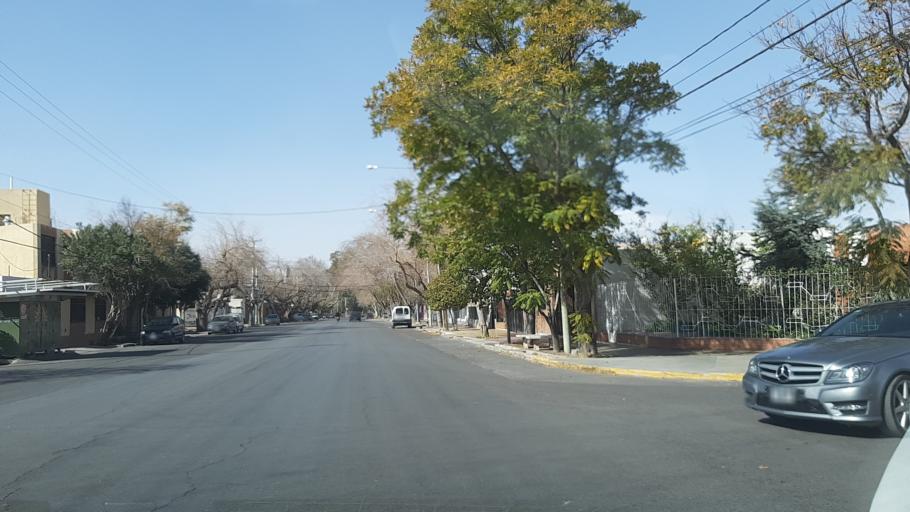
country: AR
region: San Juan
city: San Juan
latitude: -31.5281
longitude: -68.5476
